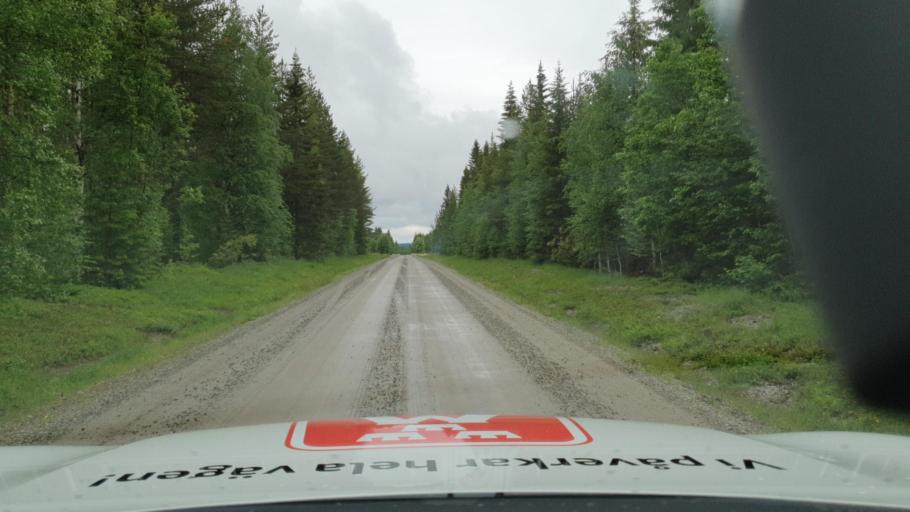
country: SE
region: Vaesterbotten
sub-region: Dorotea Kommun
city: Dorotea
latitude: 64.0813
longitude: 16.6859
